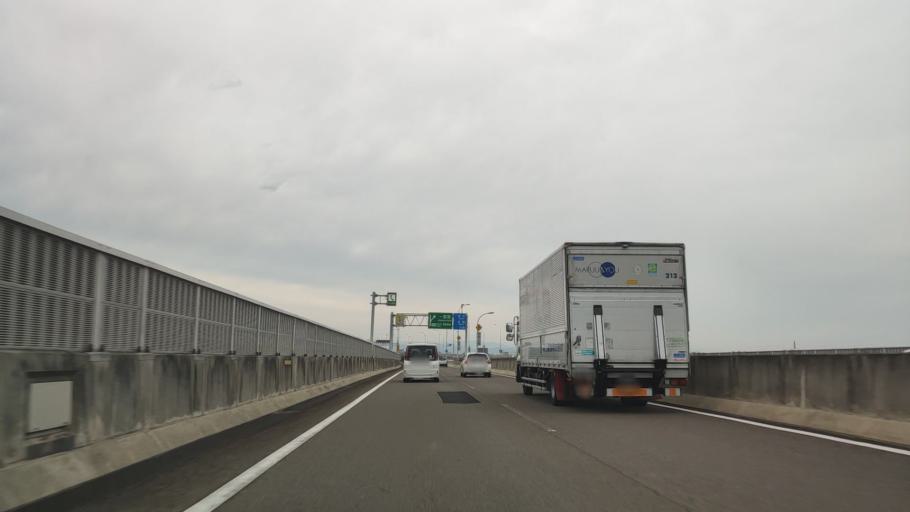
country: JP
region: Aichi
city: Iwakura
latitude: 35.2593
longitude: 136.8419
